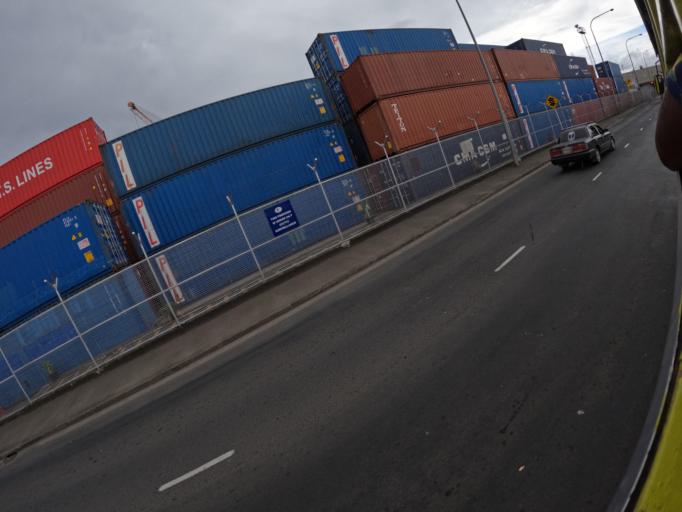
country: FJ
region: Central
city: Suva
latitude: -18.1332
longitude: 178.4252
